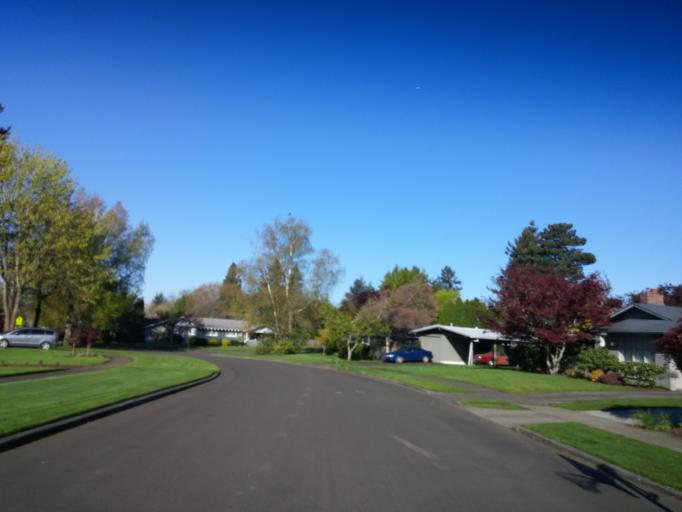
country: US
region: Oregon
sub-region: Washington County
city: West Slope
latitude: 45.5041
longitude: -122.7763
